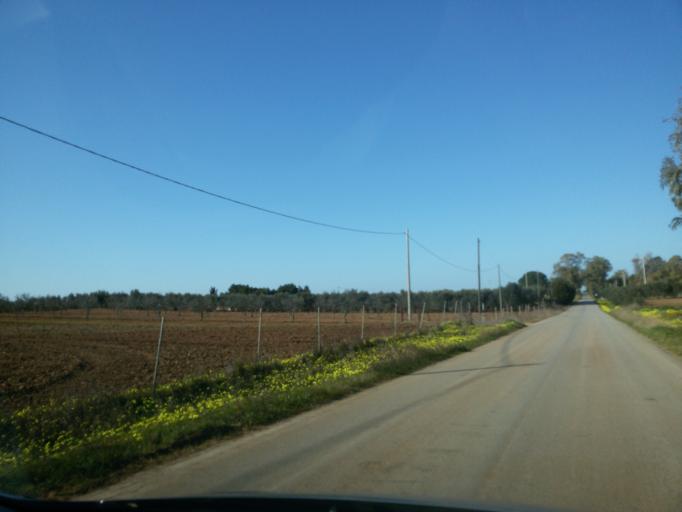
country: IT
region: Apulia
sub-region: Provincia di Brindisi
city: Mesagne
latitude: 40.6695
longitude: 17.8201
